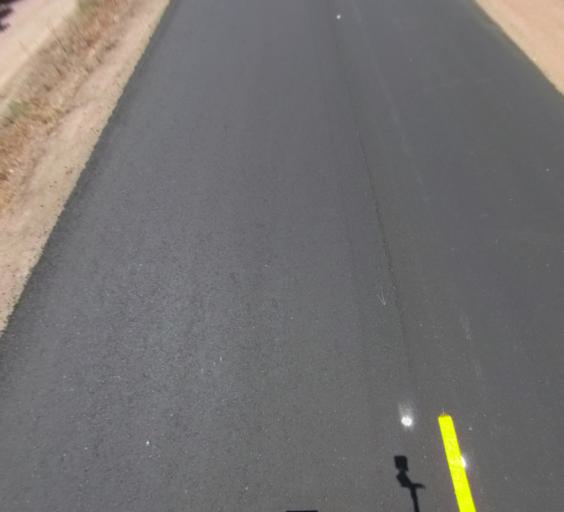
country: US
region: California
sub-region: Madera County
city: Bonadelle Ranchos-Madera Ranchos
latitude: 36.9210
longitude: -119.8579
